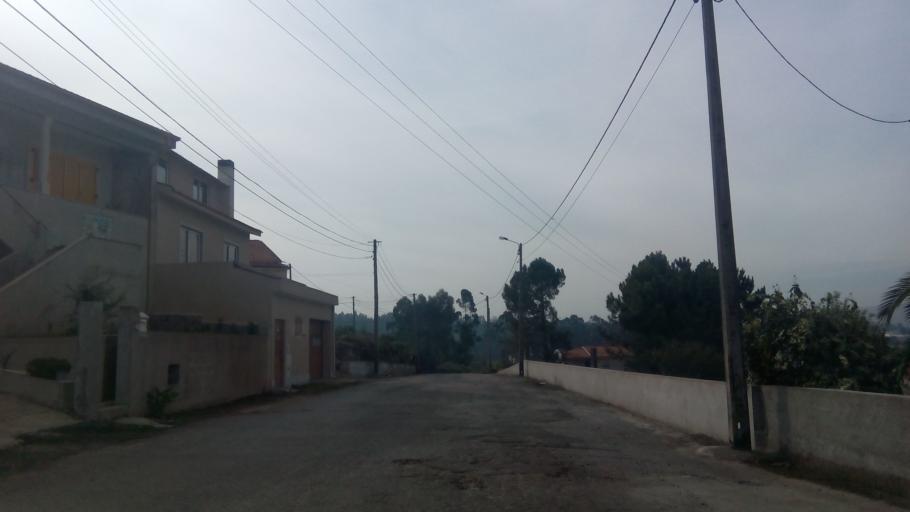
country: PT
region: Porto
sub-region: Paredes
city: Gandra
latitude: 41.1821
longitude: -8.4358
